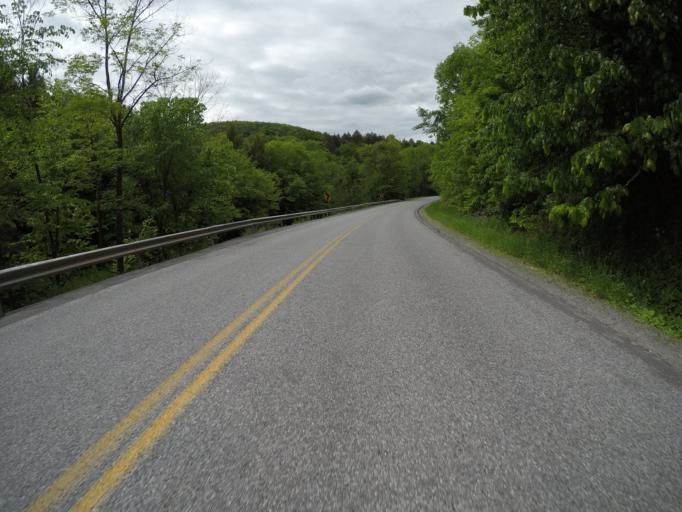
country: US
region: New York
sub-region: Delaware County
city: Stamford
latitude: 42.1819
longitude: -74.5885
